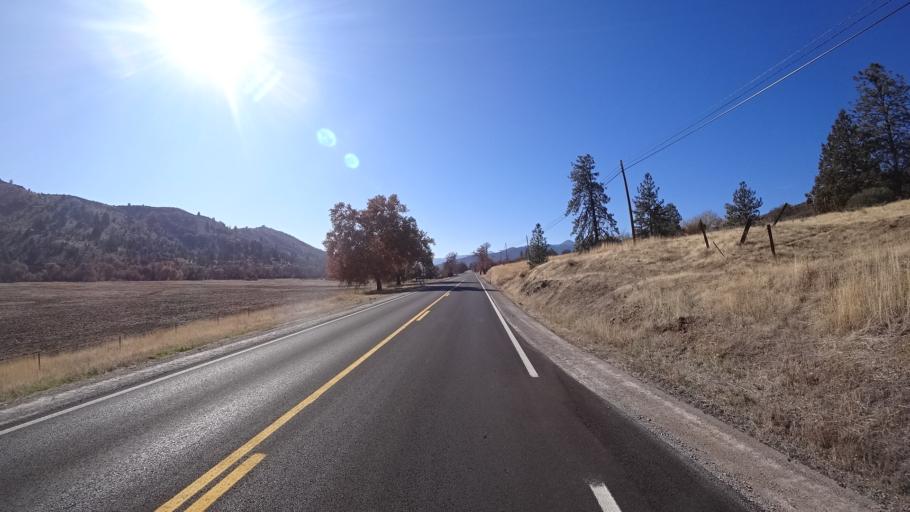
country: US
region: California
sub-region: Siskiyou County
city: Yreka
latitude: 41.7762
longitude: -122.5995
